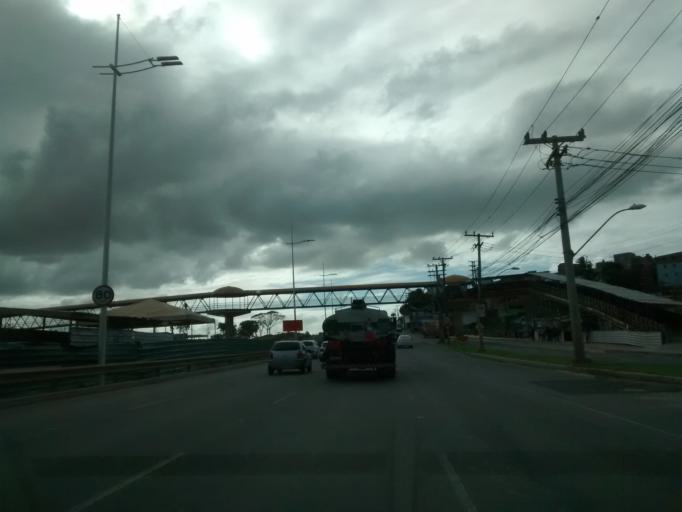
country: BR
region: Bahia
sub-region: Lauro De Freitas
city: Lauro de Freitas
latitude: -12.9259
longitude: -38.3801
